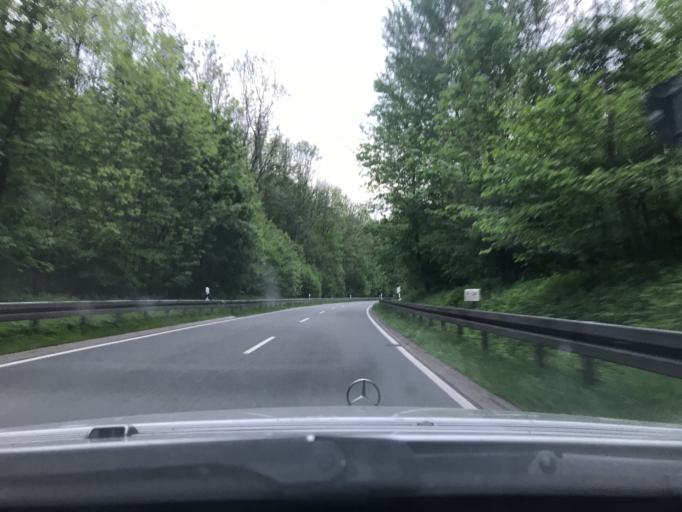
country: DE
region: Thuringia
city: Katharinenberg
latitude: 51.1836
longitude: 10.2280
